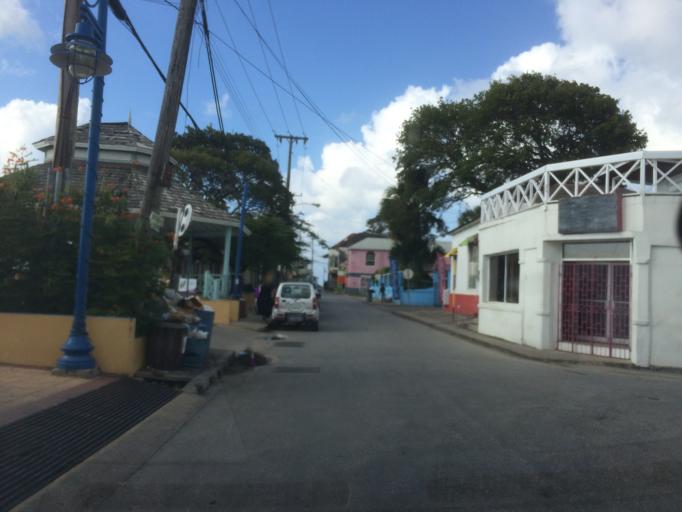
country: BB
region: Saint Peter
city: Speightstown
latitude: 13.2507
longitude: -59.6440
